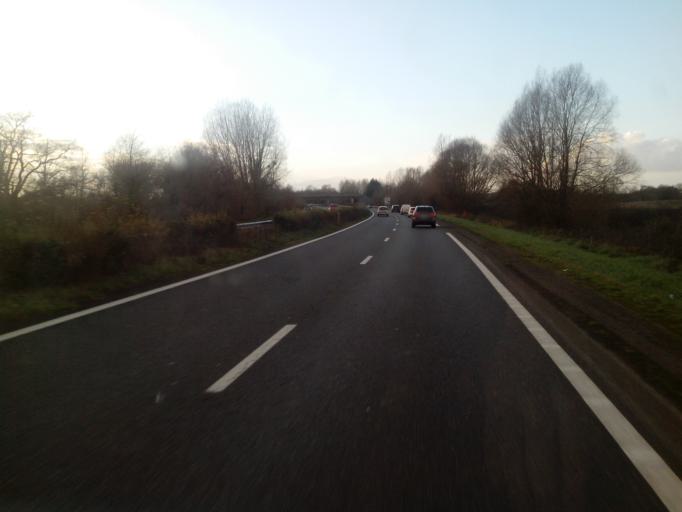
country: FR
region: Pays de la Loire
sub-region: Departement de la Loire-Atlantique
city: Mouzillon
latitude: 47.1573
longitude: -1.3003
